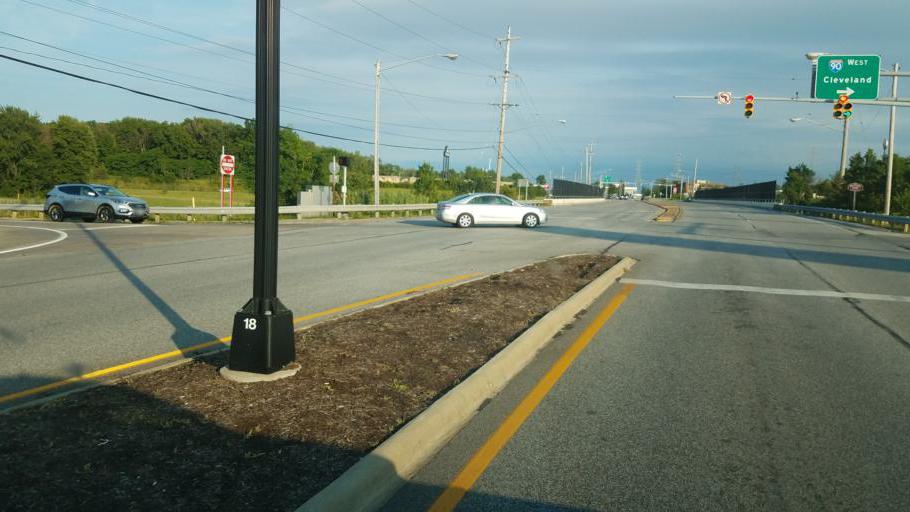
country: US
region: Ohio
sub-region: Lake County
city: Kirtland
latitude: 41.6418
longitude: -81.3748
